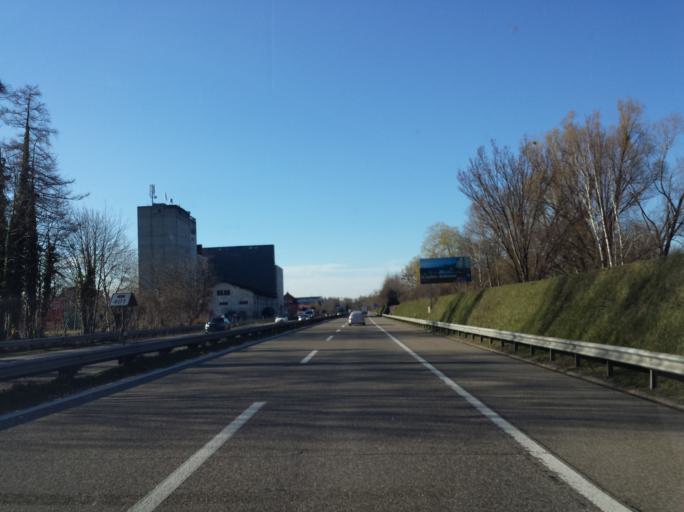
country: CH
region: Saint Gallen
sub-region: Wahlkreis Rheintal
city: Rheineck
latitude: 47.4697
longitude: 9.5899
